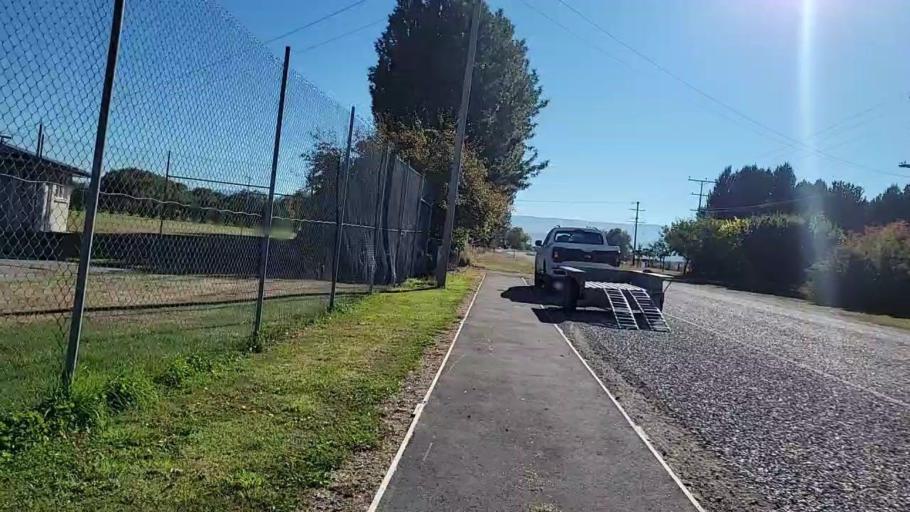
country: NZ
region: Otago
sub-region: Queenstown-Lakes District
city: Wanaka
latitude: -45.0030
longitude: 169.9168
